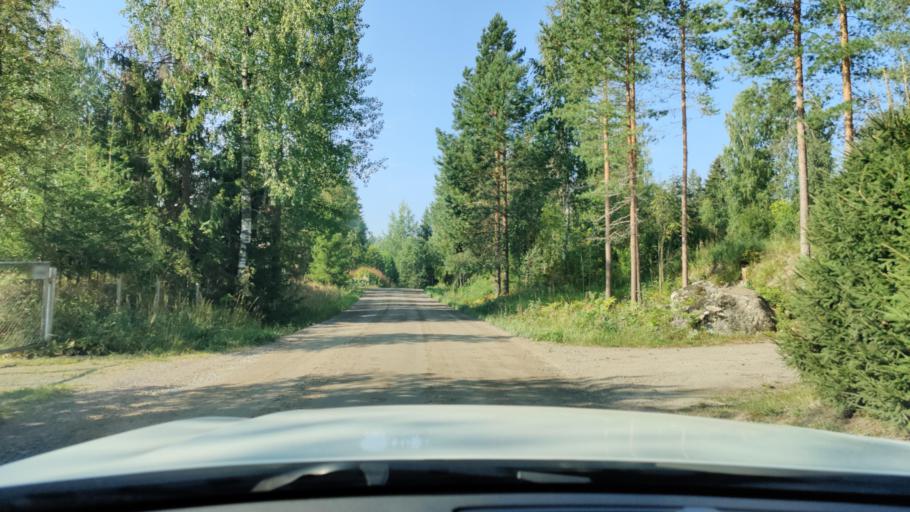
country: FI
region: Haeme
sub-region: Riihimaeki
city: Loppi
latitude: 60.6762
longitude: 24.5736
